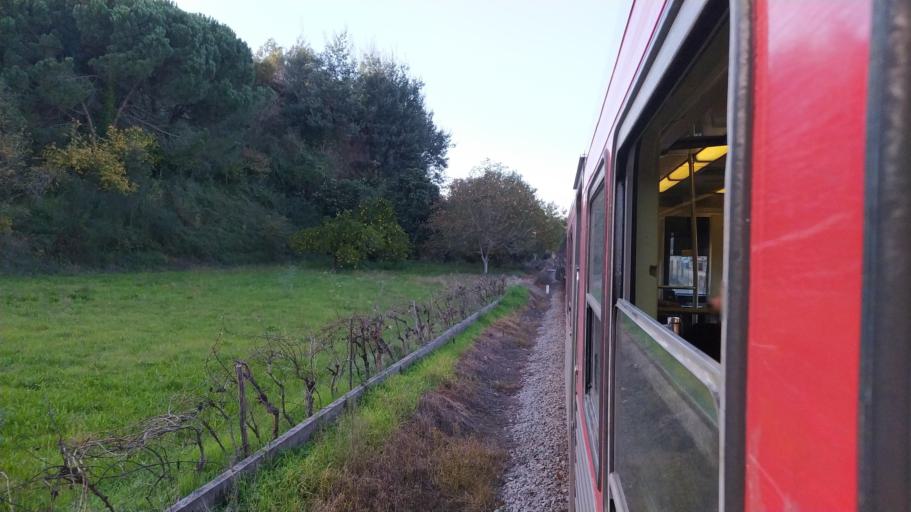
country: PT
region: Aveiro
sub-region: Aveiro
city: Eixo
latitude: 40.6119
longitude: -8.5343
